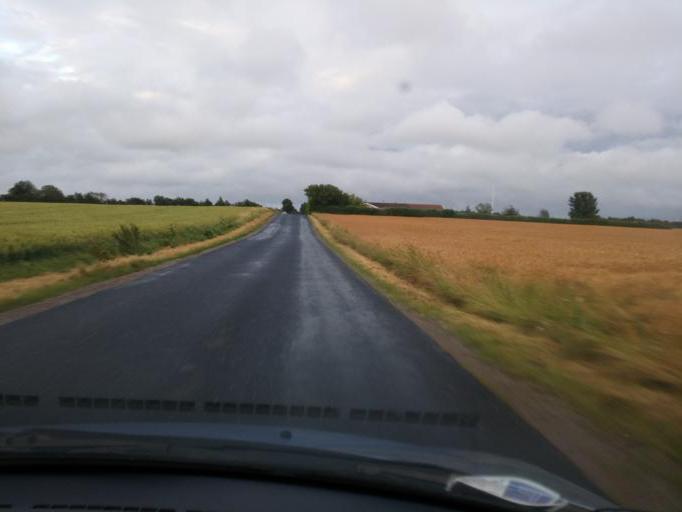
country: DK
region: South Denmark
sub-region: Kerteminde Kommune
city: Kerteminde
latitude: 55.5071
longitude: 10.6296
